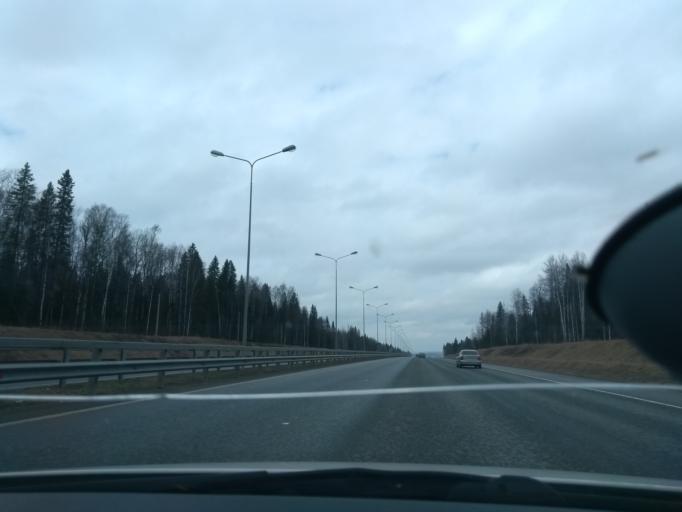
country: RU
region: Perm
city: Zvezdnyy
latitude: 57.7550
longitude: 56.3333
